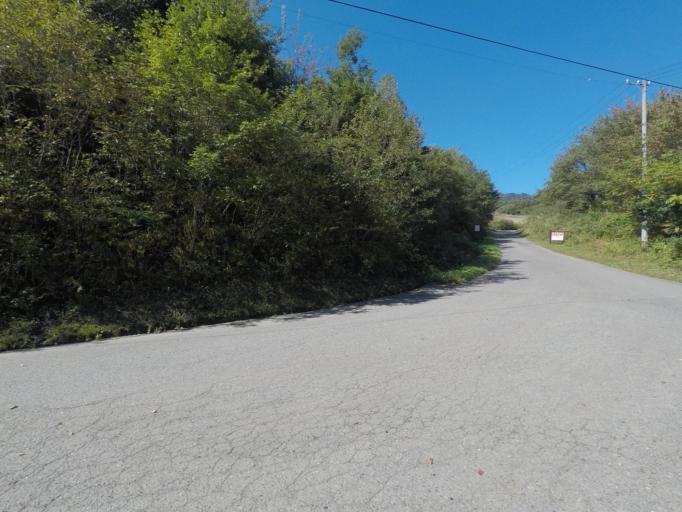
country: JP
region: Nagano
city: Tatsuno
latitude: 35.9741
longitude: 137.7421
